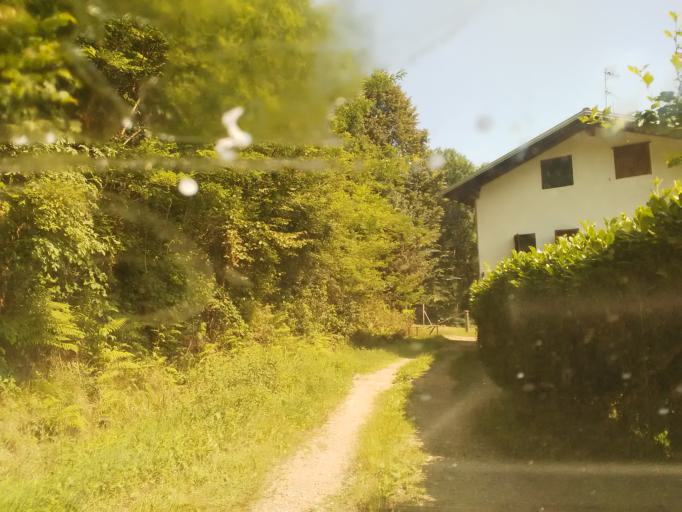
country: IT
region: Piedmont
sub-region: Provincia di Biella
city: Pray
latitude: 45.6810
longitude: 8.2262
